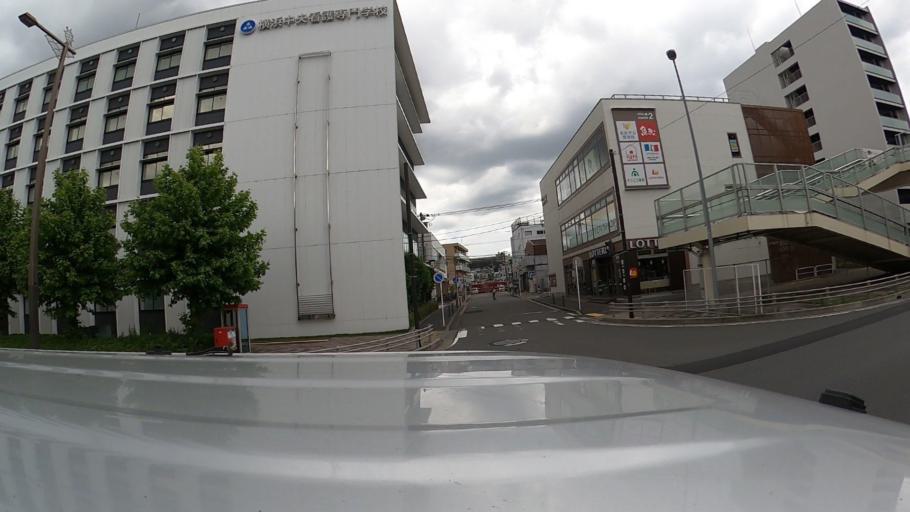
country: JP
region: Kanagawa
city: Yokohama
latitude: 35.4803
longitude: 139.6401
